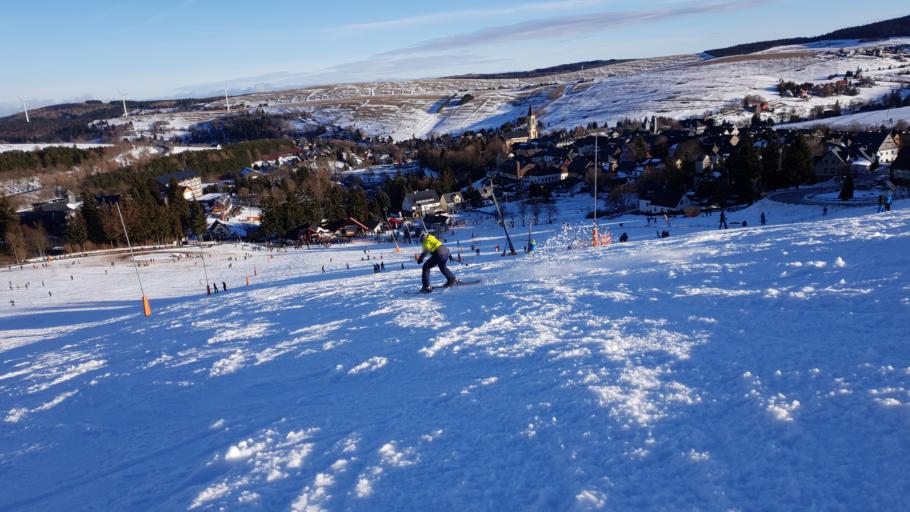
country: DE
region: Saxony
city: Kurort Oberwiesenthal
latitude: 50.4217
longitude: 12.9634
